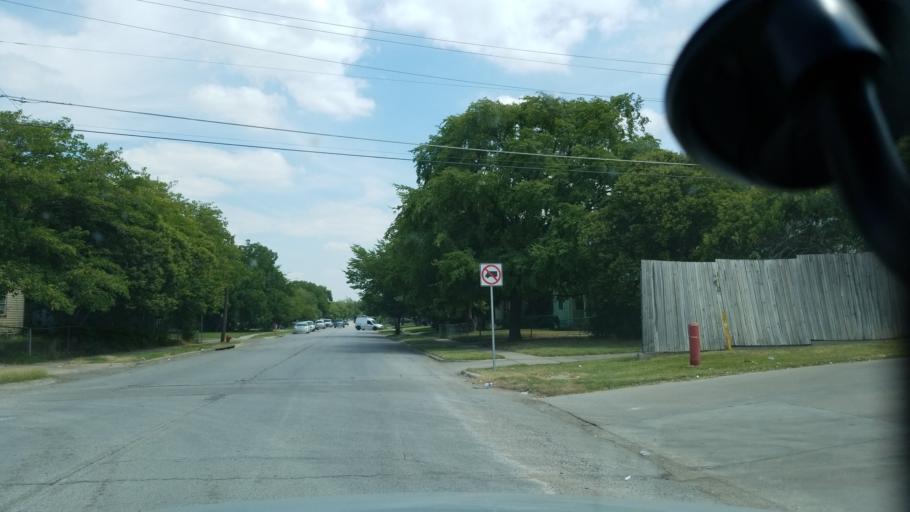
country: US
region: Texas
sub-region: Dallas County
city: Grand Prairie
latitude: 32.7507
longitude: -96.9780
